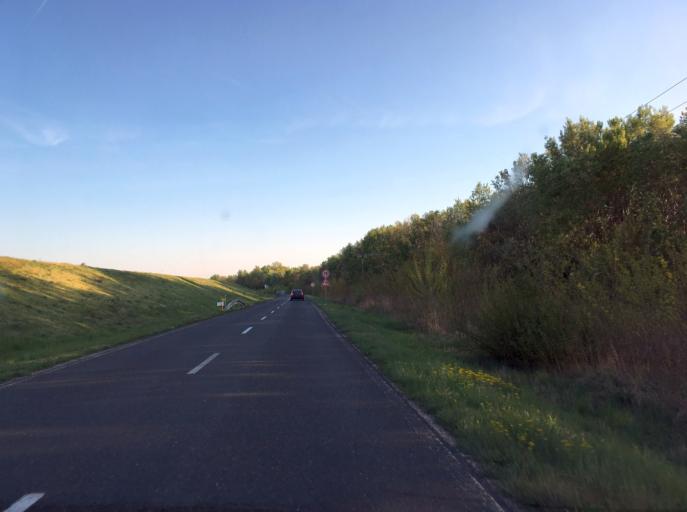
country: HU
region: Gyor-Moson-Sopron
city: Rajka
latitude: 48.0105
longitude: 17.2519
